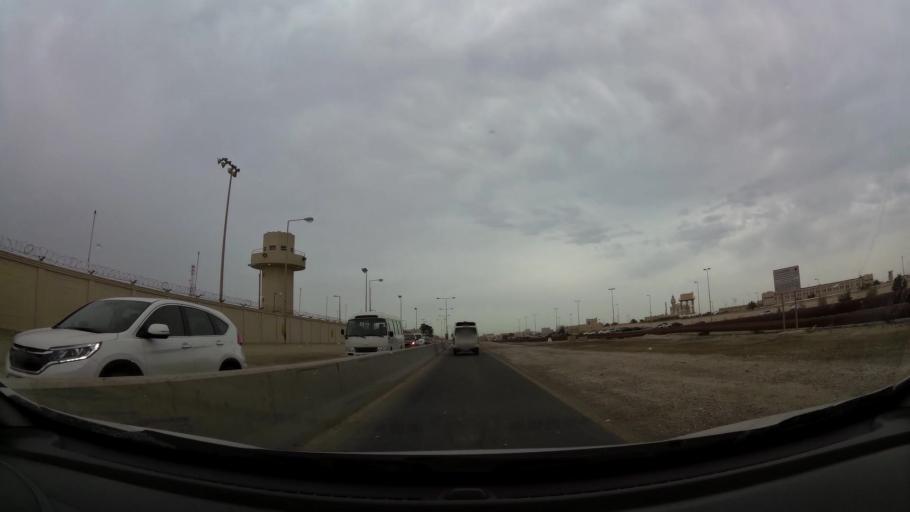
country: BH
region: Central Governorate
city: Madinat Hamad
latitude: 26.1533
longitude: 50.4829
